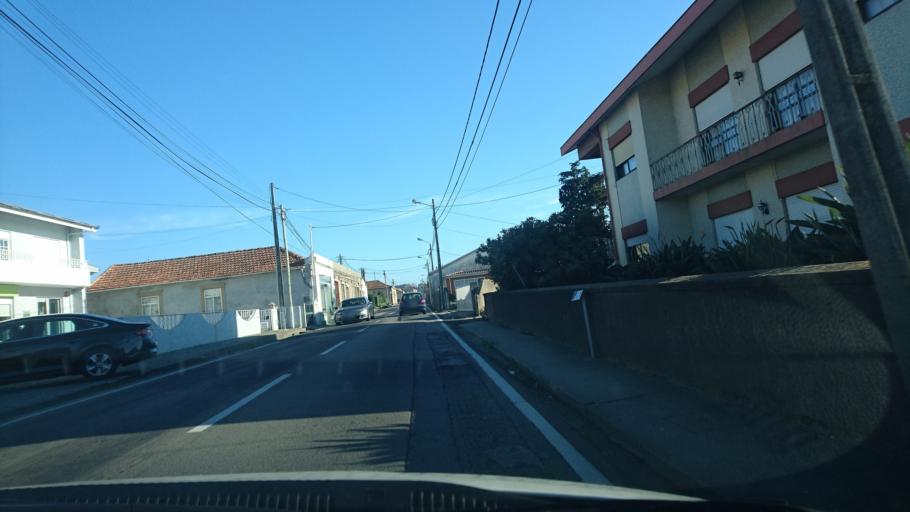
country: PT
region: Aveiro
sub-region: Espinho
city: Silvalde
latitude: 40.9954
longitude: -8.6332
